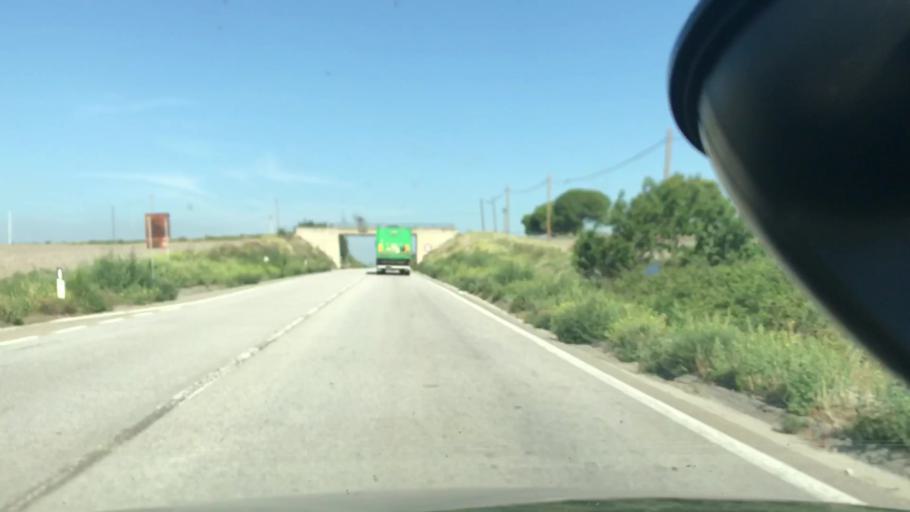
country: IT
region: Apulia
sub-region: Provincia di Foggia
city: Candela
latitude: 41.1123
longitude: 15.5833
